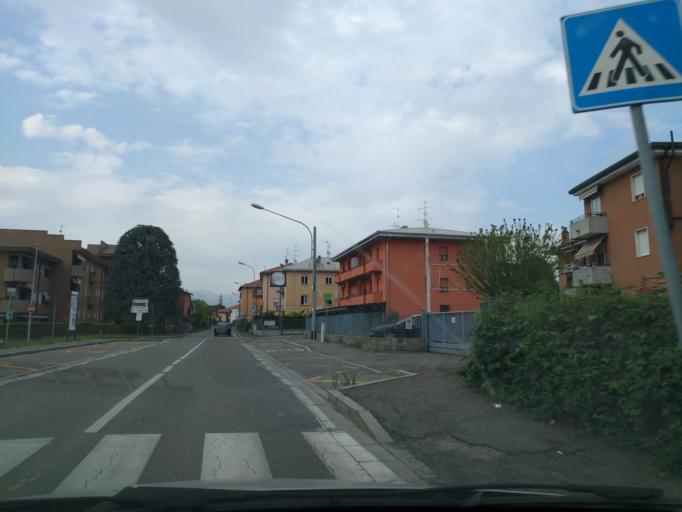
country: IT
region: Lombardy
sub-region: Provincia di Como
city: Cantu
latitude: 45.7253
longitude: 9.1507
